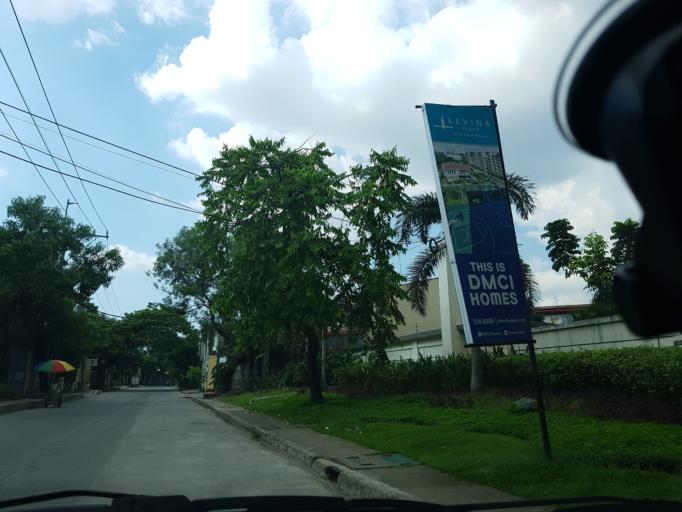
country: PH
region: Calabarzon
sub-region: Province of Rizal
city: Cainta
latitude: 14.5815
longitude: 121.0919
